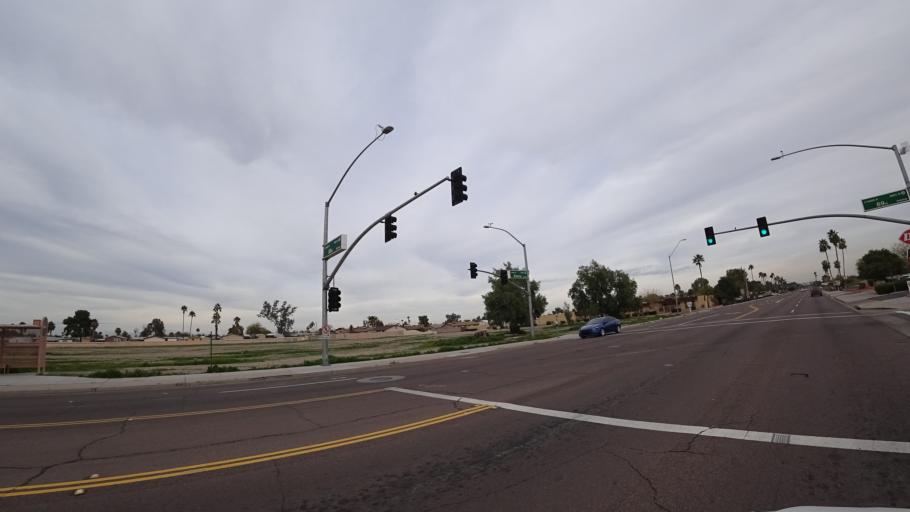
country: US
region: Arizona
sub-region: Maricopa County
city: Peoria
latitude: 33.5808
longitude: -112.2509
